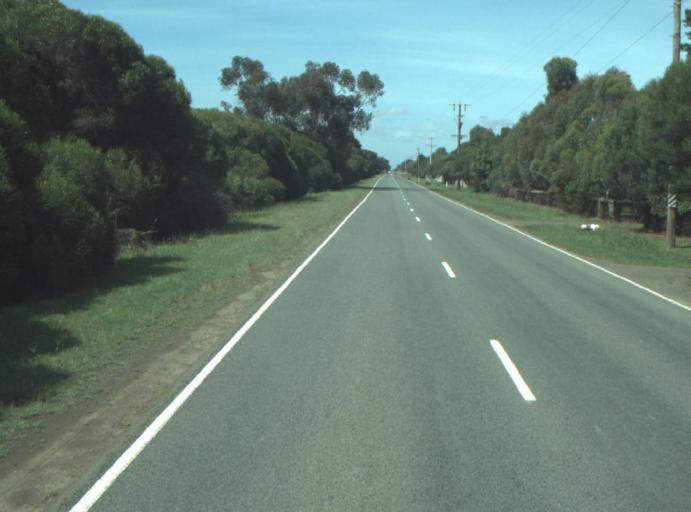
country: AU
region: Victoria
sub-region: Greater Geelong
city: Lara
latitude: -38.0441
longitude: 144.4297
